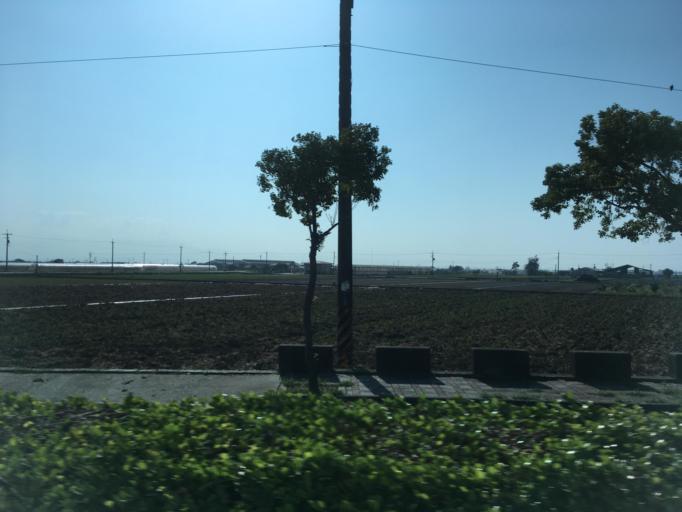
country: TW
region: Taiwan
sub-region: Chiayi
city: Taibao
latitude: 23.4790
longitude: 120.3432
